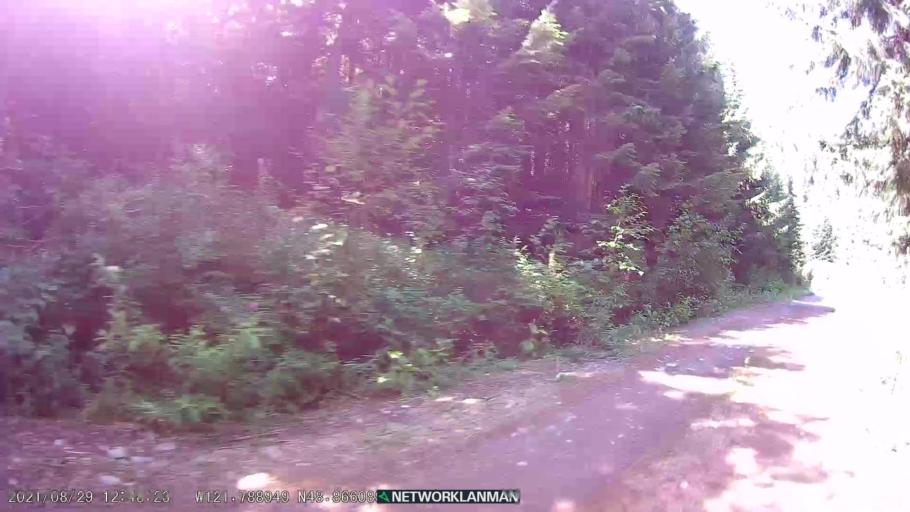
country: CA
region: British Columbia
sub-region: Fraser Valley Regional District
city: Chilliwack
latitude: 48.8656
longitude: -121.7884
